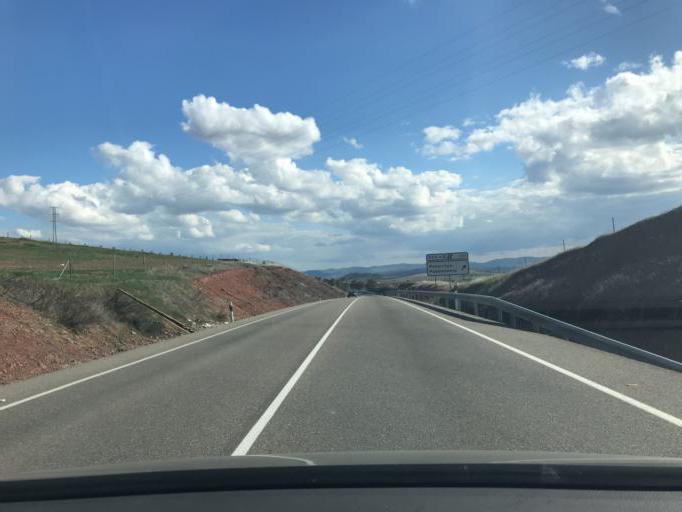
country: ES
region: Andalusia
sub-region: Province of Cordoba
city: Penarroya-Pueblonuevo
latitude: 38.3043
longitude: -5.2570
